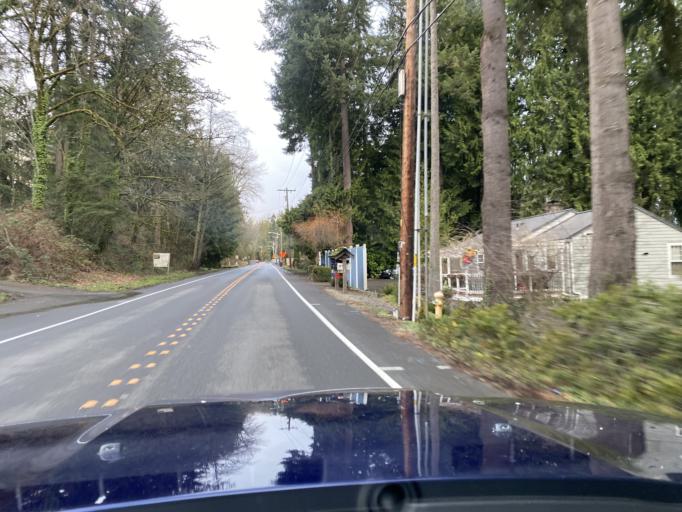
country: US
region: Washington
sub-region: King County
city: West Lake Sammamish
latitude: 47.5710
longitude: -122.1164
